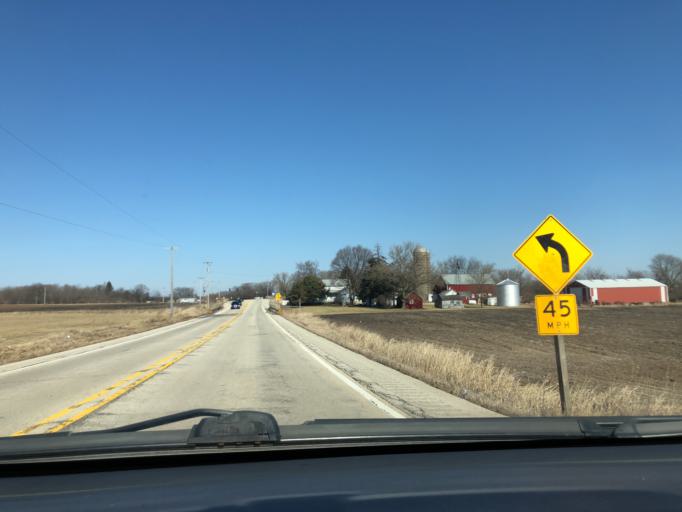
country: US
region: Illinois
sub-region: Kane County
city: Hampshire
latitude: 42.1192
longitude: -88.4816
